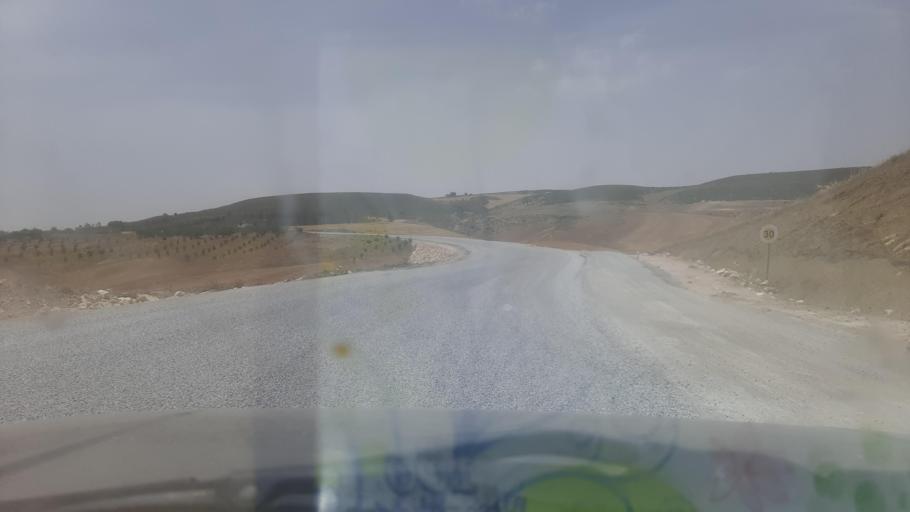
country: TN
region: Tunis
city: La Mohammedia
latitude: 36.5481
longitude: 10.1535
